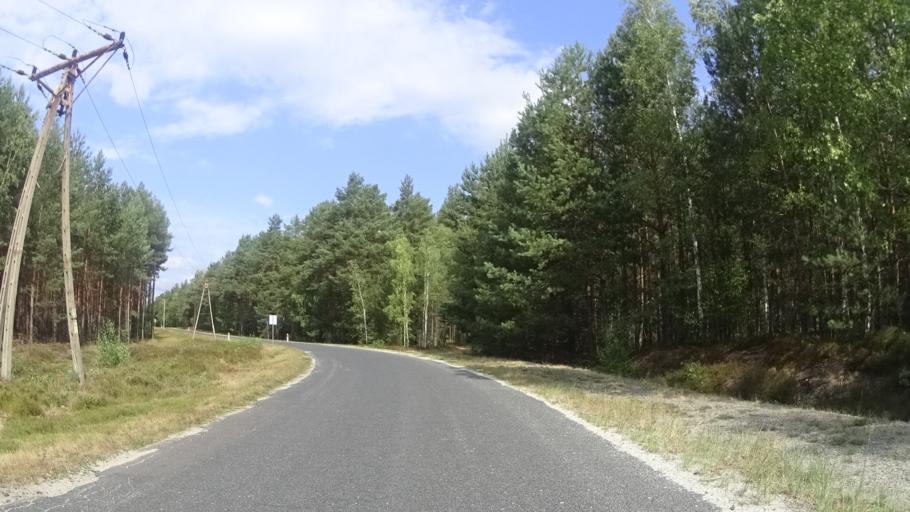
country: PL
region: Lubusz
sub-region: Powiat zarski
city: Leknica
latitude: 51.5284
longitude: 14.8191
